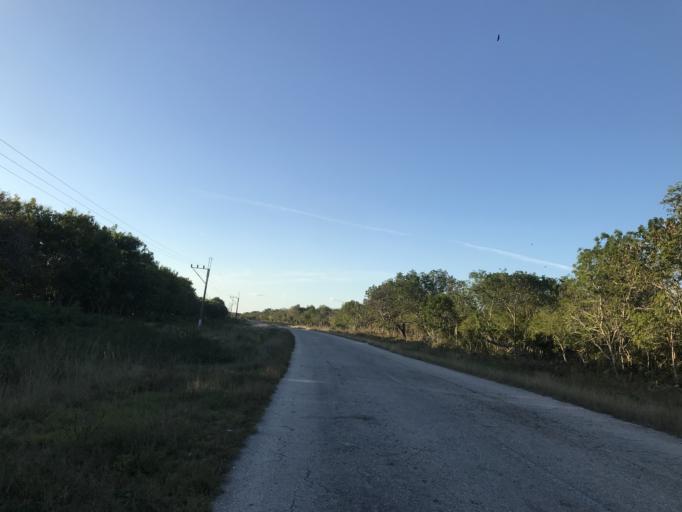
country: CU
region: Cienfuegos
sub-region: Municipio de Aguada de Pasajeros
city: Aguada de Pasajeros
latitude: 22.0726
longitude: -81.0562
